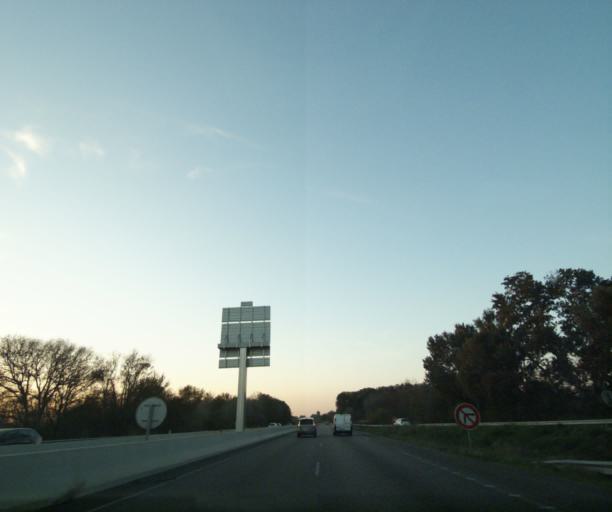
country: FR
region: Provence-Alpes-Cote d'Azur
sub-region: Departement des Bouches-du-Rhone
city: Saint-Martin-de-Crau
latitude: 43.6345
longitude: 4.7392
